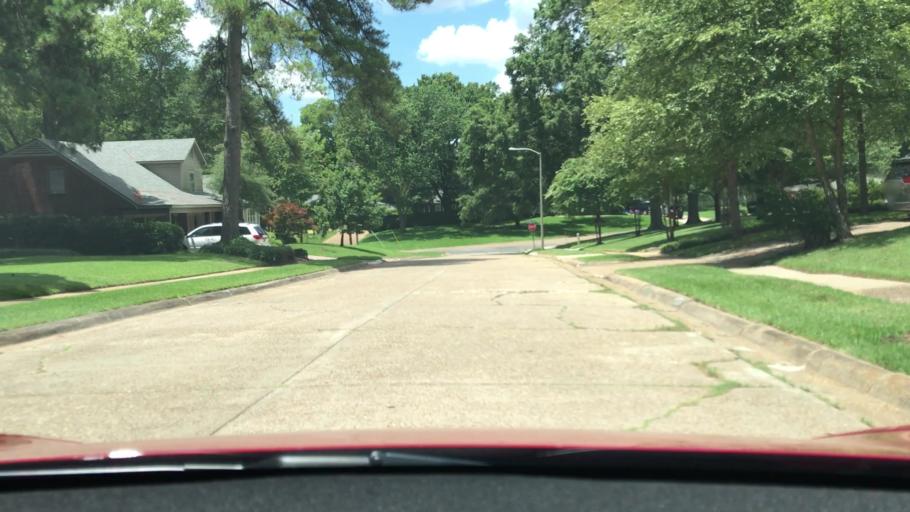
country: US
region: Louisiana
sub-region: Bossier Parish
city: Bossier City
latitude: 32.4590
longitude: -93.7527
